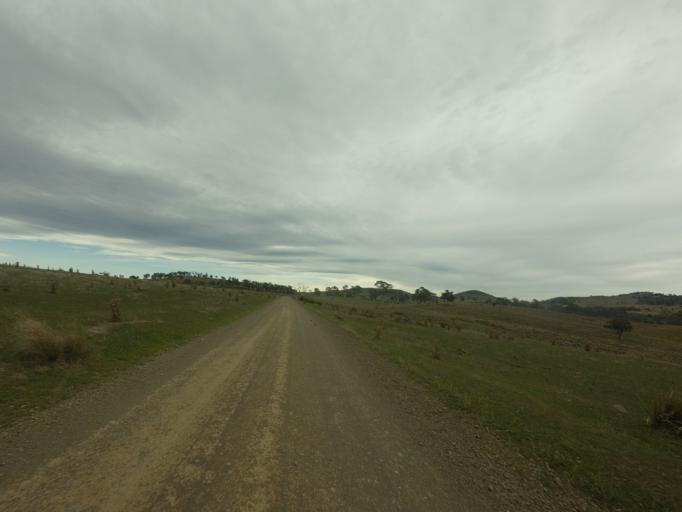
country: AU
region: Tasmania
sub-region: Derwent Valley
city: New Norfolk
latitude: -42.3921
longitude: 146.8935
